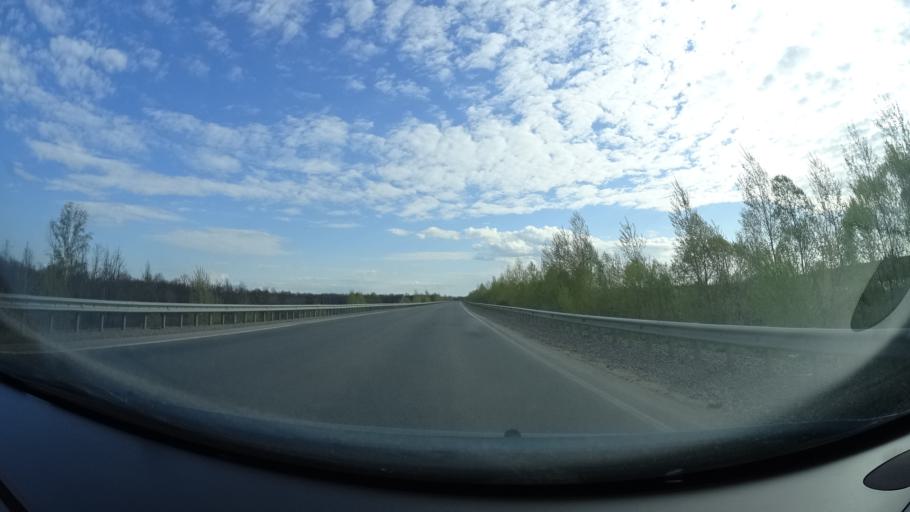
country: RU
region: Bashkortostan
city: Blagoveshchensk
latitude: 55.0197
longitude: 55.7877
